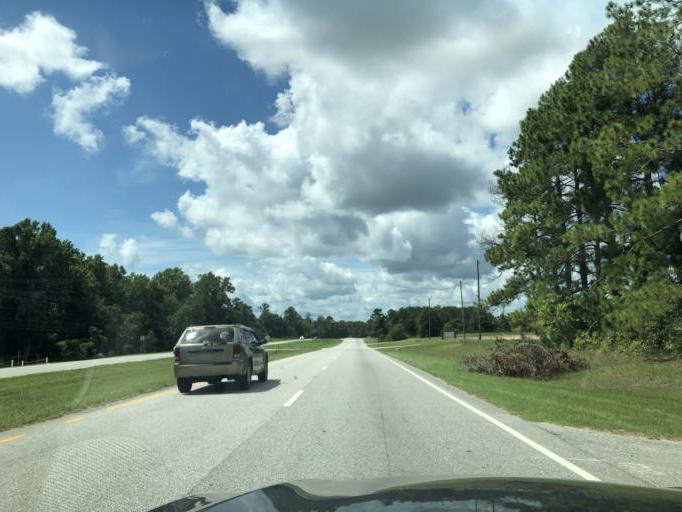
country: US
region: Alabama
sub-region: Barbour County
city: Eufaula
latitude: 31.9478
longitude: -85.1257
